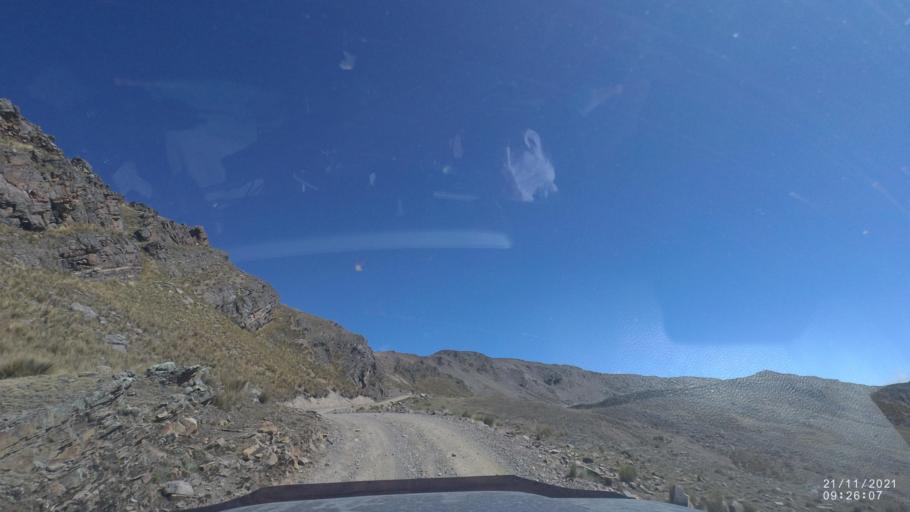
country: BO
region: Cochabamba
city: Cochabamba
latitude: -17.0887
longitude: -66.2545
